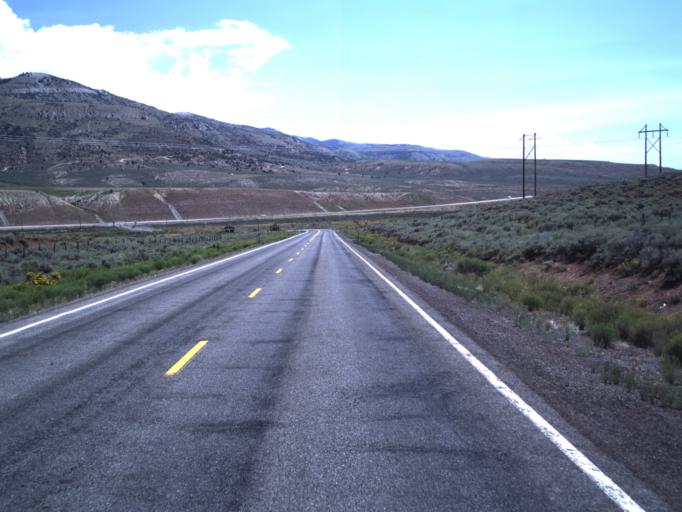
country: US
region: Utah
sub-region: Carbon County
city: Helper
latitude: 39.8607
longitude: -111.0372
